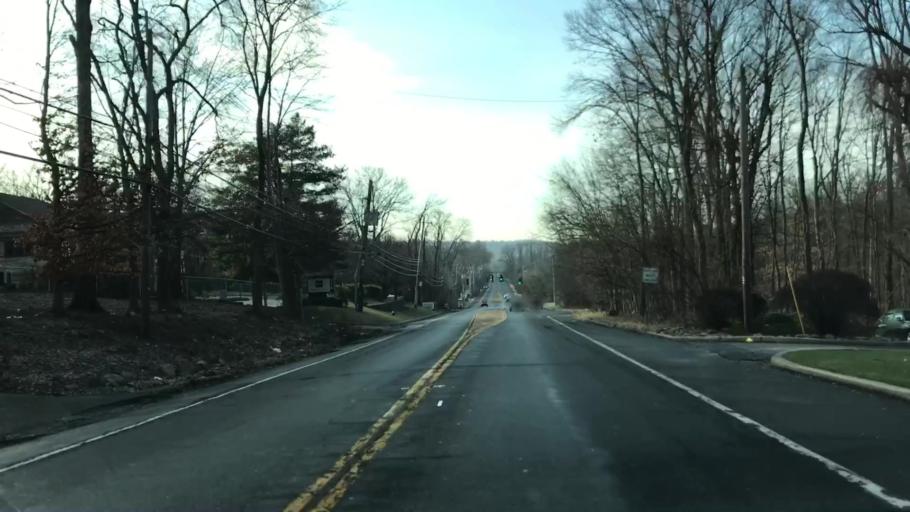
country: US
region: New York
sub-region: Rockland County
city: Valley Cottage
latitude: 41.1304
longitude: -73.9402
